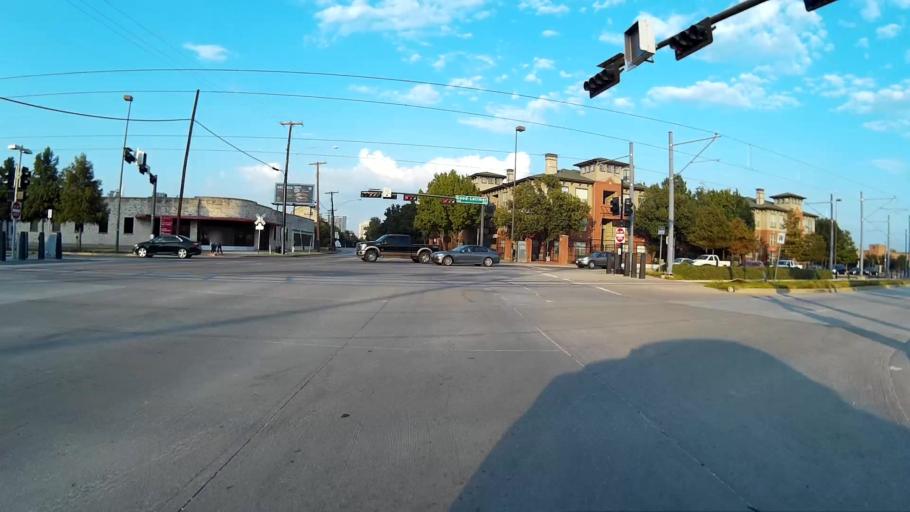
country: US
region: Texas
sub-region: Dallas County
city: Dallas
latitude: 32.7852
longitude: -96.7881
